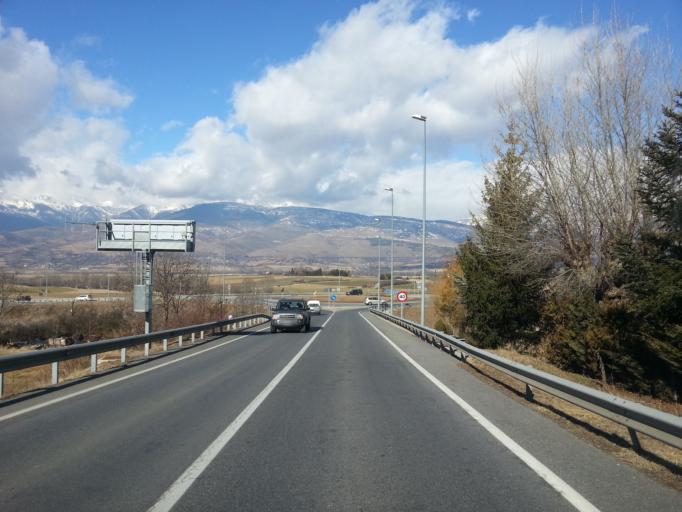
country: ES
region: Catalonia
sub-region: Provincia de Girona
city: Alp
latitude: 42.3703
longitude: 1.8813
